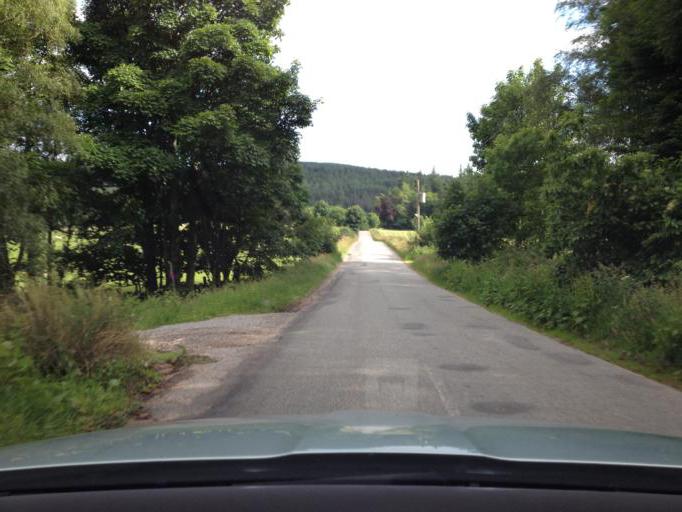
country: GB
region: Scotland
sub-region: Aberdeenshire
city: Banchory
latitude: 56.9697
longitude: -2.5784
